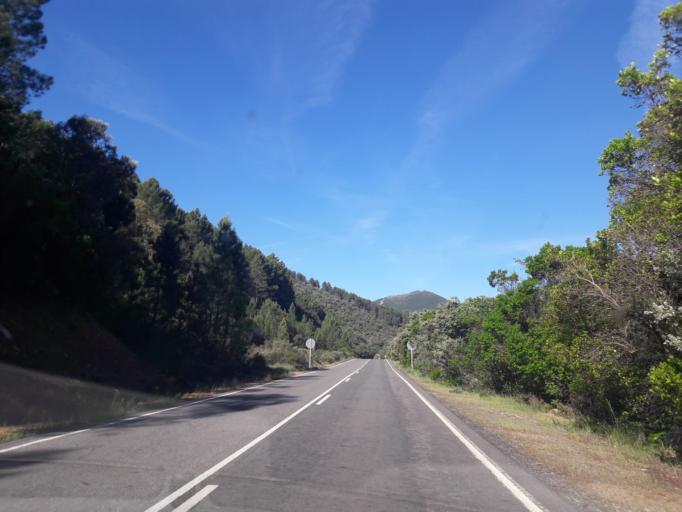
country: ES
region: Castille and Leon
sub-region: Provincia de Salamanca
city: Sotoserrano
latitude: 40.4056
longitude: -6.0596
